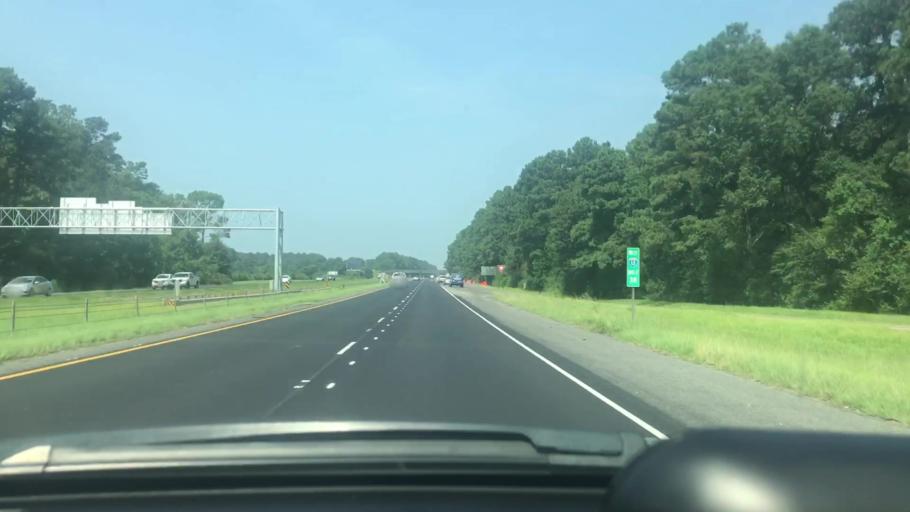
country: US
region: Louisiana
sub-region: Tangipahoa Parish
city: Hammond
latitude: 30.4792
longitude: -90.4928
